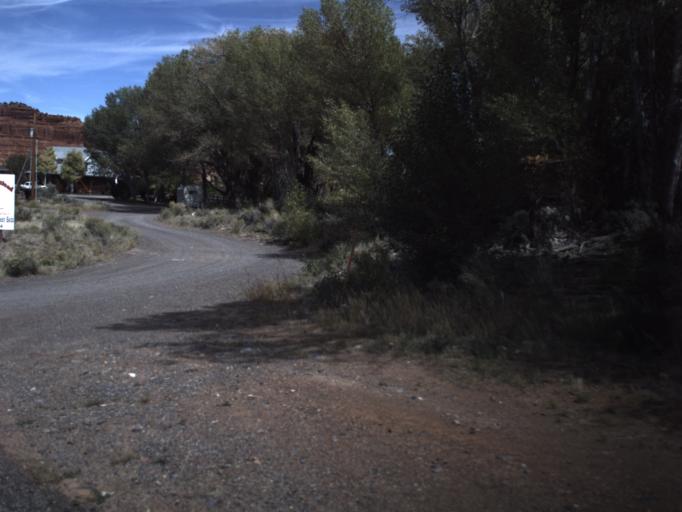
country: US
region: Utah
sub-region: Wayne County
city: Loa
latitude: 38.2589
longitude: -111.3763
